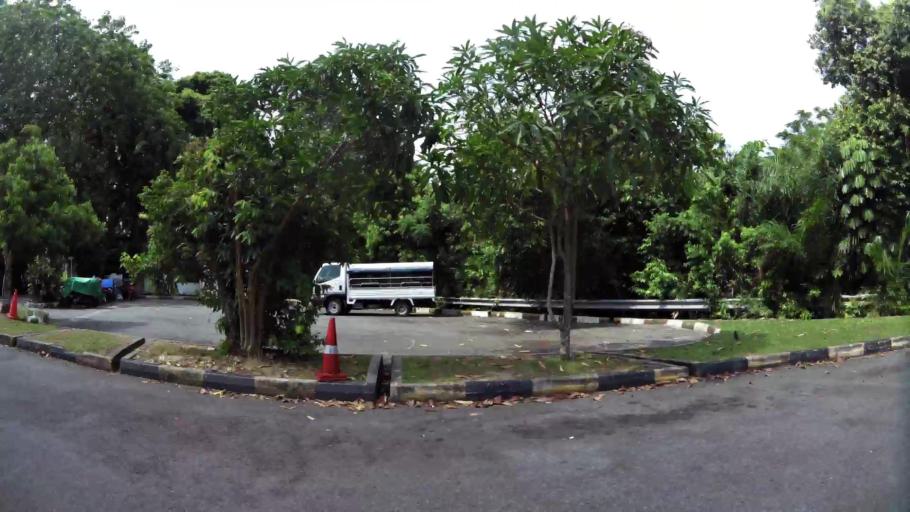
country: SG
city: Singapore
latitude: 1.3352
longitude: 103.7916
